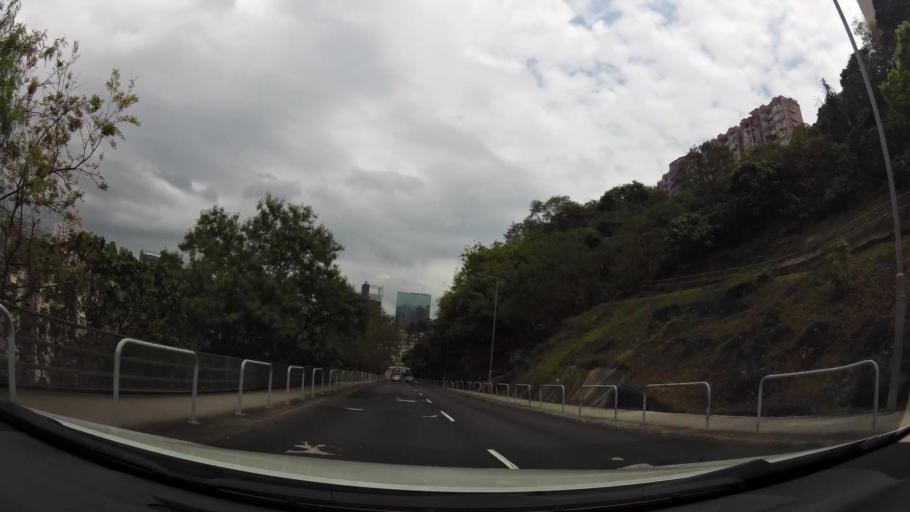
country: HK
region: Wanchai
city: Wan Chai
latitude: 22.2886
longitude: 114.2042
